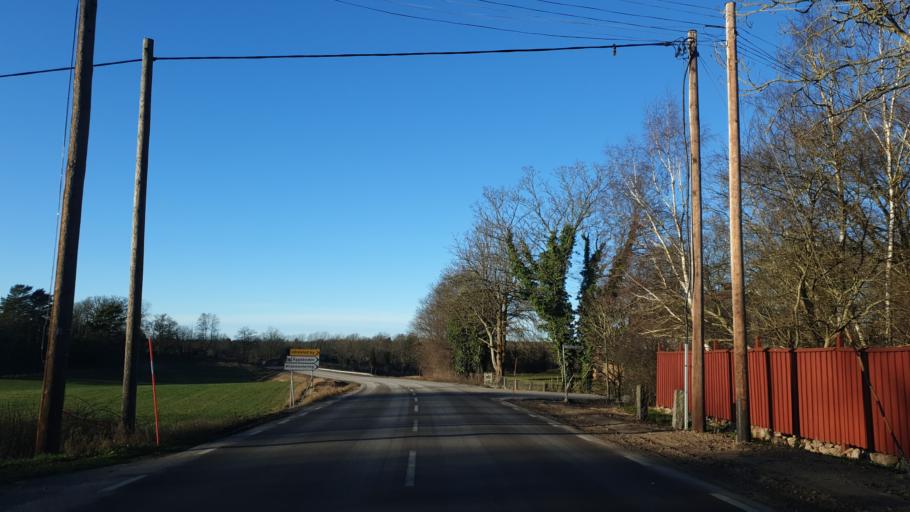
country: SE
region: Blekinge
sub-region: Ronneby Kommun
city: Ronneby
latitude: 56.1972
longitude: 15.3309
